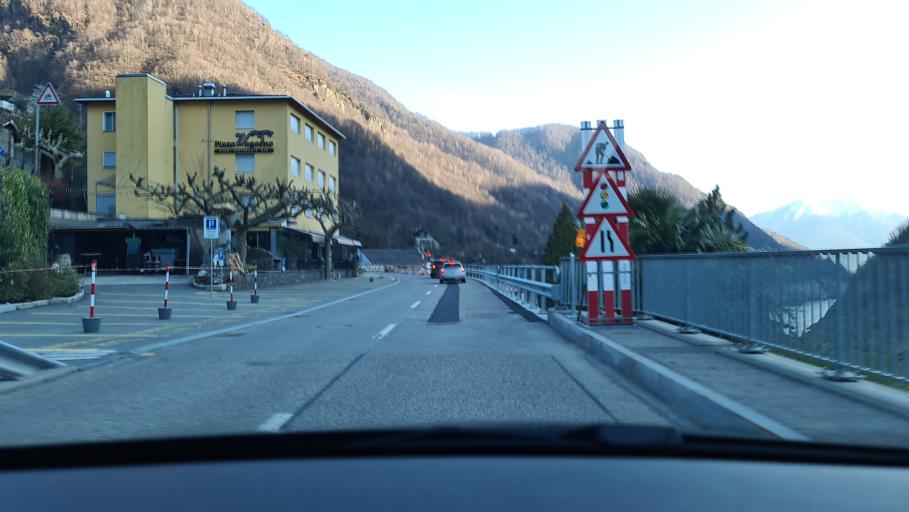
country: CH
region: Ticino
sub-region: Locarno District
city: Gordola
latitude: 46.2223
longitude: 8.8583
